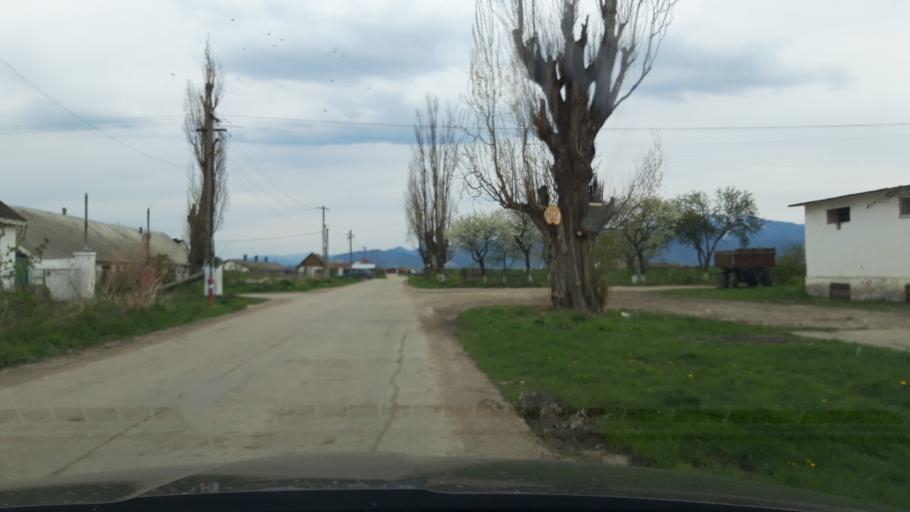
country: RO
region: Brasov
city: Codlea
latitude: 45.6990
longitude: 25.4609
